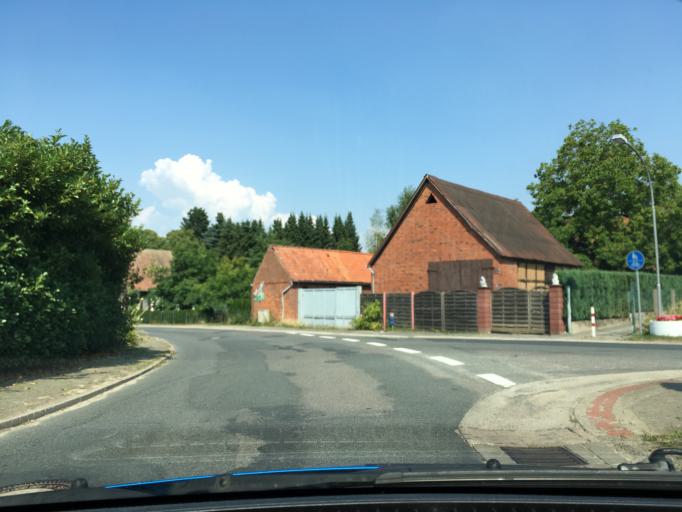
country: DE
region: Lower Saxony
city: Tosterglope
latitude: 53.2433
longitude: 10.7807
